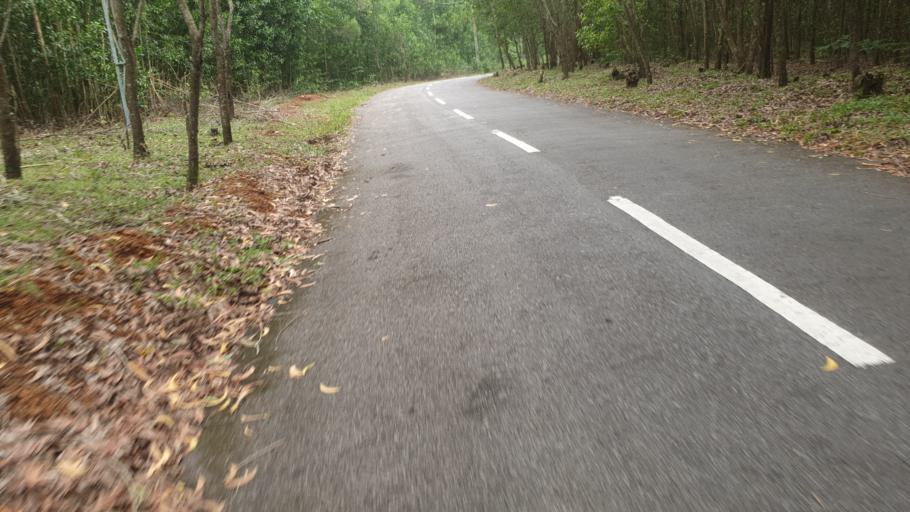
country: IN
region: Kerala
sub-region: Thiruvananthapuram
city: Nedumangad
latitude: 8.6321
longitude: 77.1196
